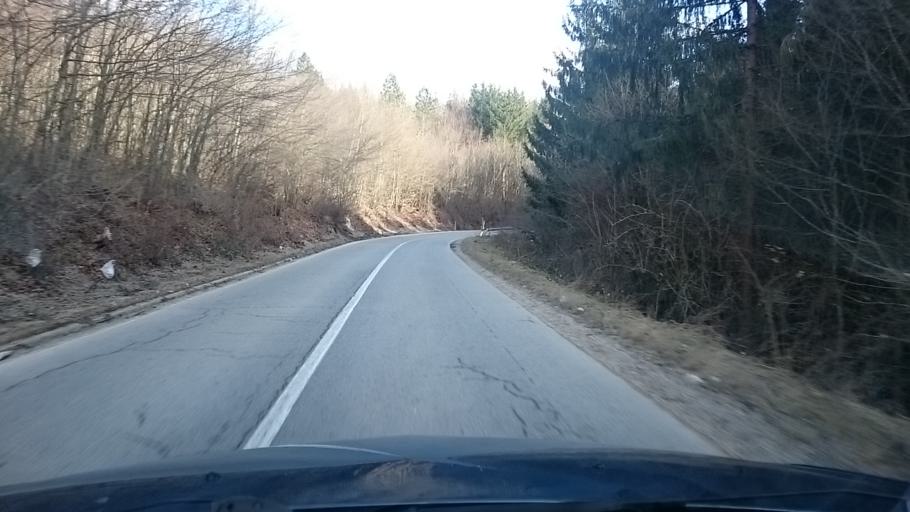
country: BA
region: Republika Srpska
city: Starcevica
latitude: 44.6727
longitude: 17.2210
